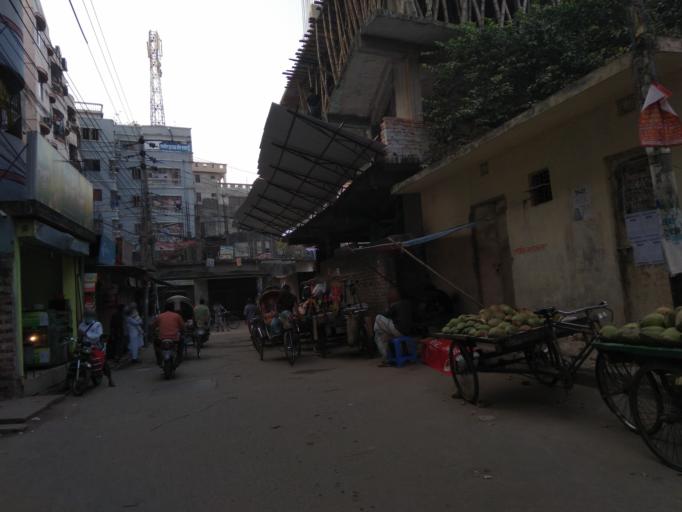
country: BD
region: Dhaka
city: Azimpur
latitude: 23.7265
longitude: 90.3730
